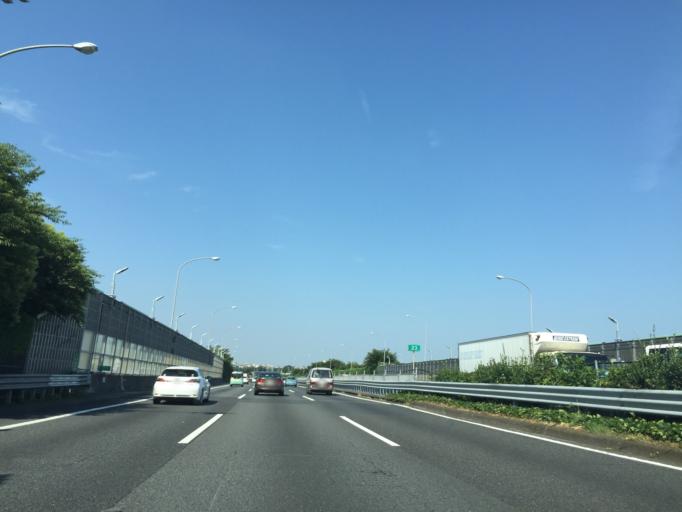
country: JP
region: Kanagawa
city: Minami-rinkan
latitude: 35.4845
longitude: 139.4628
